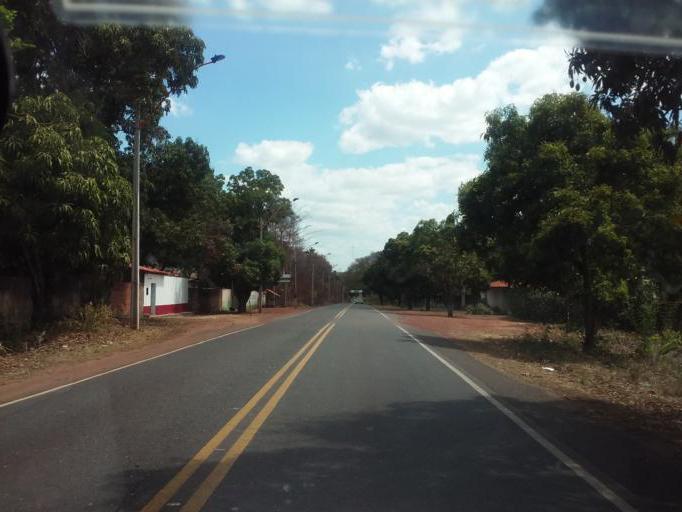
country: BR
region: Piaui
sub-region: Teresina
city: Teresina
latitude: -5.0516
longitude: -42.6849
